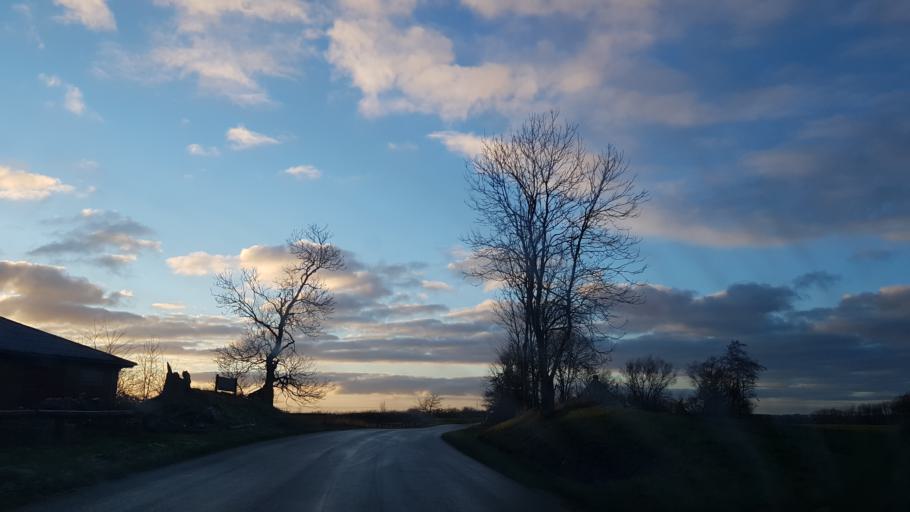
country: DK
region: South Denmark
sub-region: Kolding Kommune
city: Vamdrup
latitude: 55.3742
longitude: 9.2952
